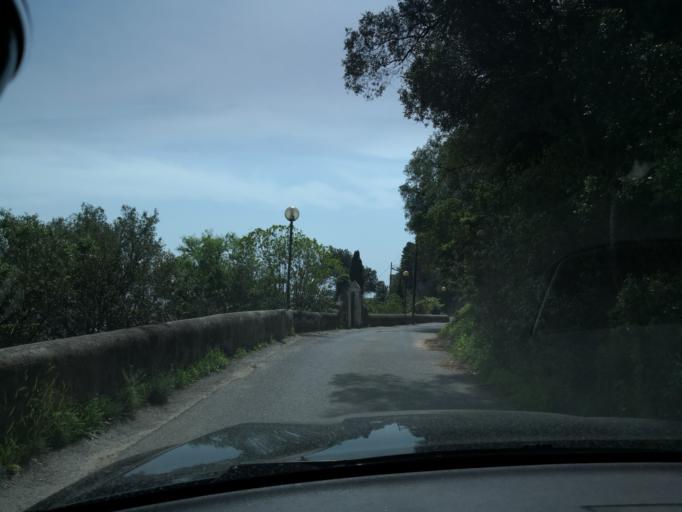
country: PT
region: Setubal
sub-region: Palmela
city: Quinta do Anjo
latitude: 38.4746
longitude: -8.9837
